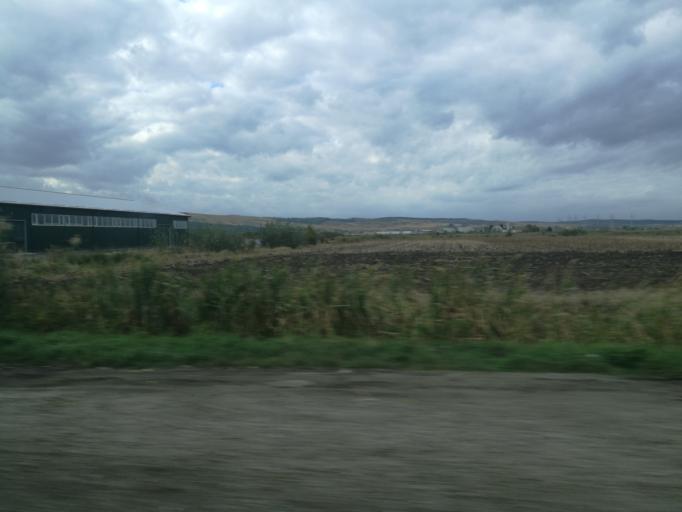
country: RO
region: Mures
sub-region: Comuna Cristesti
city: Cristesti
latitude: 46.4938
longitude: 24.4746
